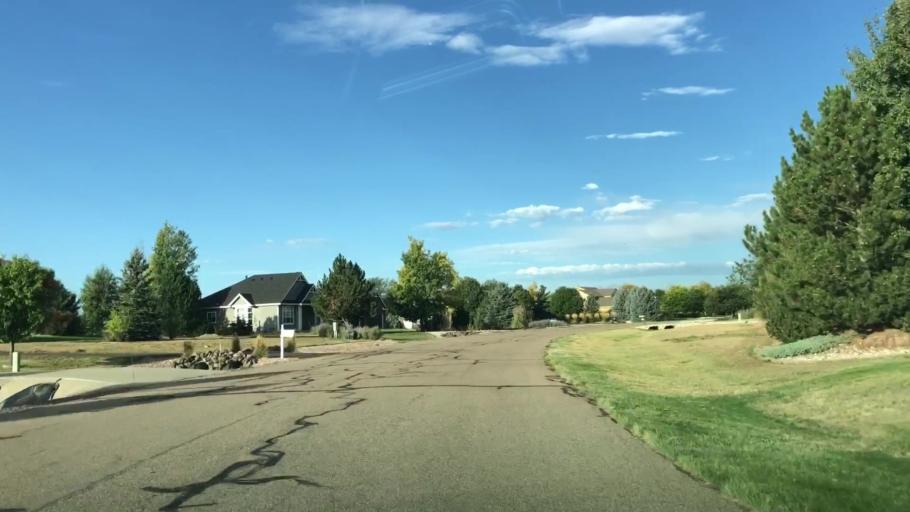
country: US
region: Colorado
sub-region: Weld County
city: Windsor
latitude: 40.4379
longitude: -104.9477
